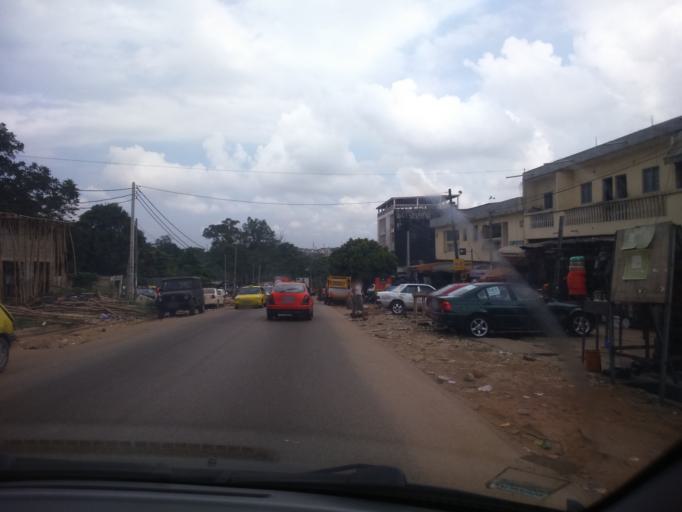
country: CI
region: Lagunes
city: Abobo
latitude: 5.3661
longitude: -4.0129
